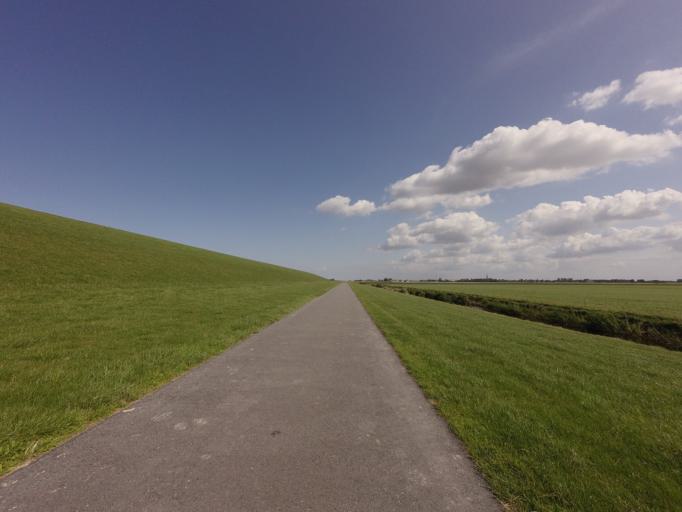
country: NL
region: Friesland
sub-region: Gemeente Dongeradeel
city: Holwerd
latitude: 53.3727
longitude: 5.8683
